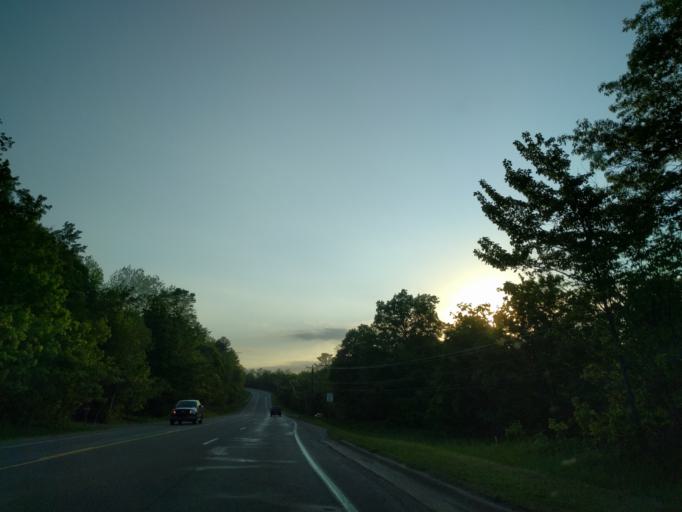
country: US
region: Michigan
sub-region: Marquette County
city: Trowbridge Park
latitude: 46.5649
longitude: -87.4418
